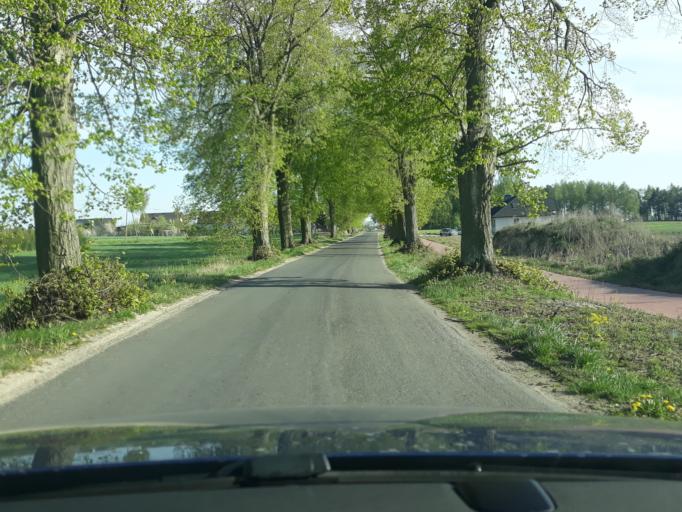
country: PL
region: Pomeranian Voivodeship
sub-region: Powiat czluchowski
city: Przechlewo
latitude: 53.8348
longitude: 17.3674
